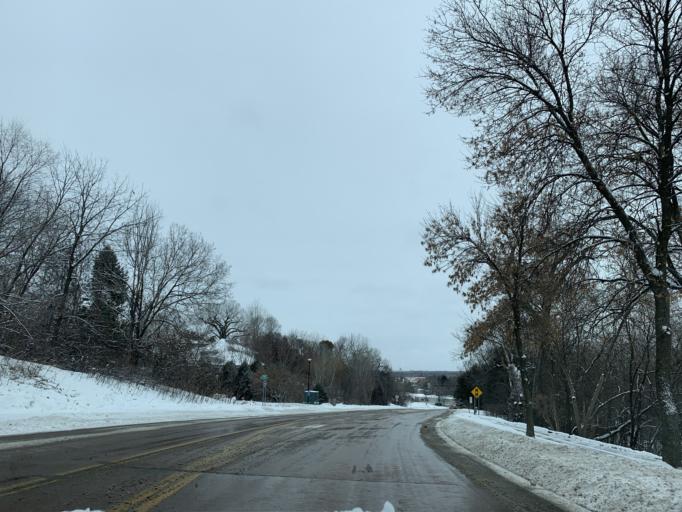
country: US
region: Minnesota
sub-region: Carver County
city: Chaska
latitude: 44.7864
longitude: -93.6122
